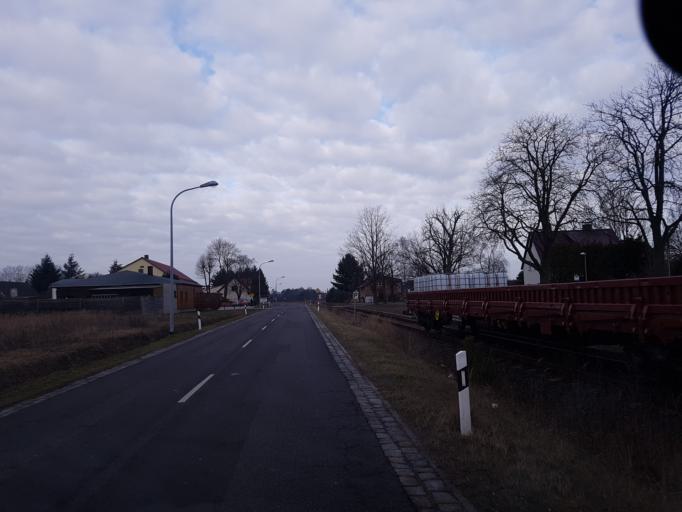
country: DE
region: Brandenburg
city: Finsterwalde
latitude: 51.6132
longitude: 13.7609
